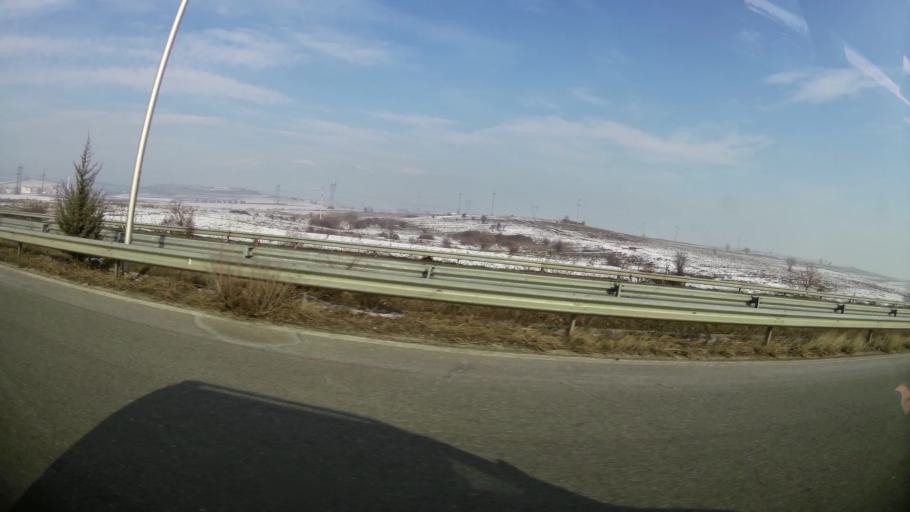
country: MK
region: Butel
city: Butel
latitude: 42.0358
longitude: 21.4690
